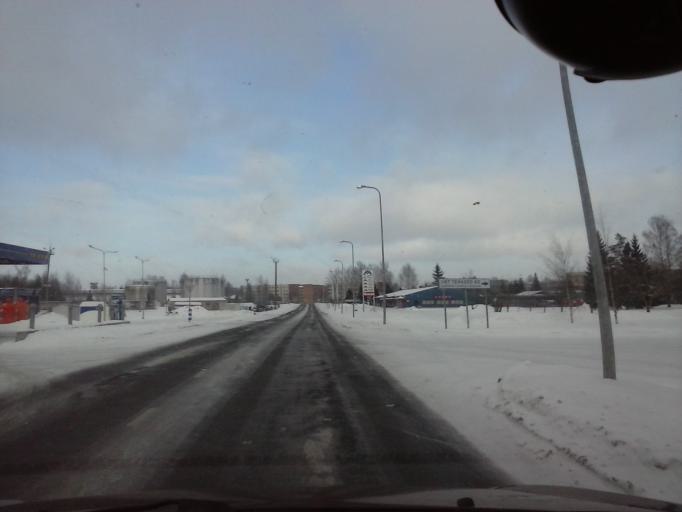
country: EE
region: Viljandimaa
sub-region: Viljandi linn
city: Viljandi
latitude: 58.3535
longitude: 25.5739
